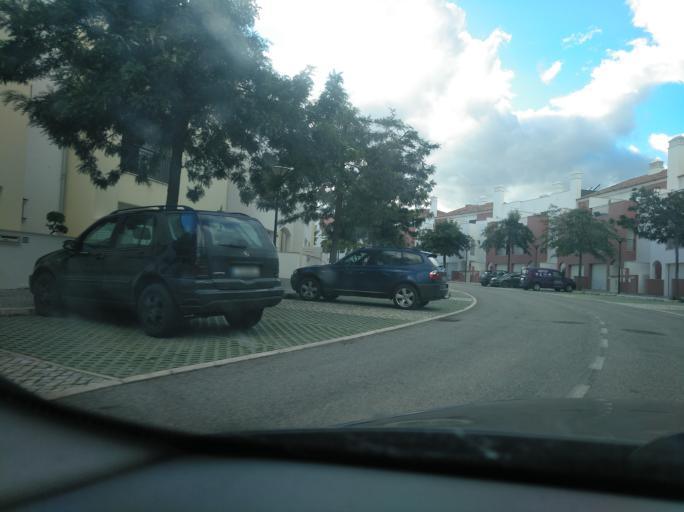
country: PT
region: Faro
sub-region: Tavira
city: Tavira
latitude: 37.1426
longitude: -7.6064
